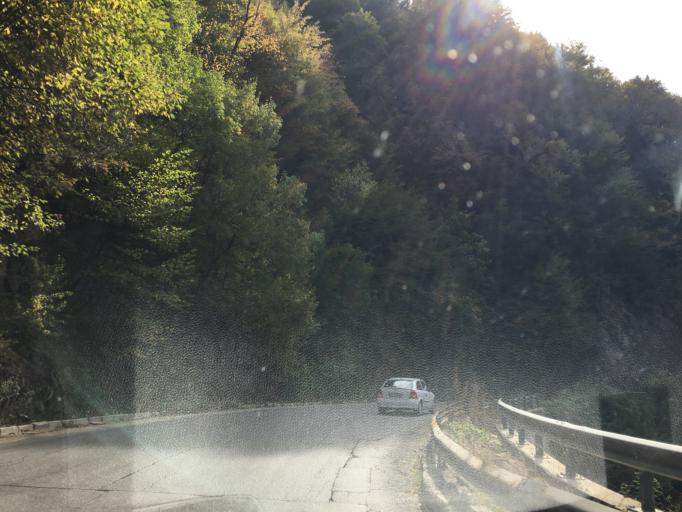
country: BG
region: Pazardzhik
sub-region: Obshtina Batak
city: Batak
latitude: 41.9769
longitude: 24.2431
